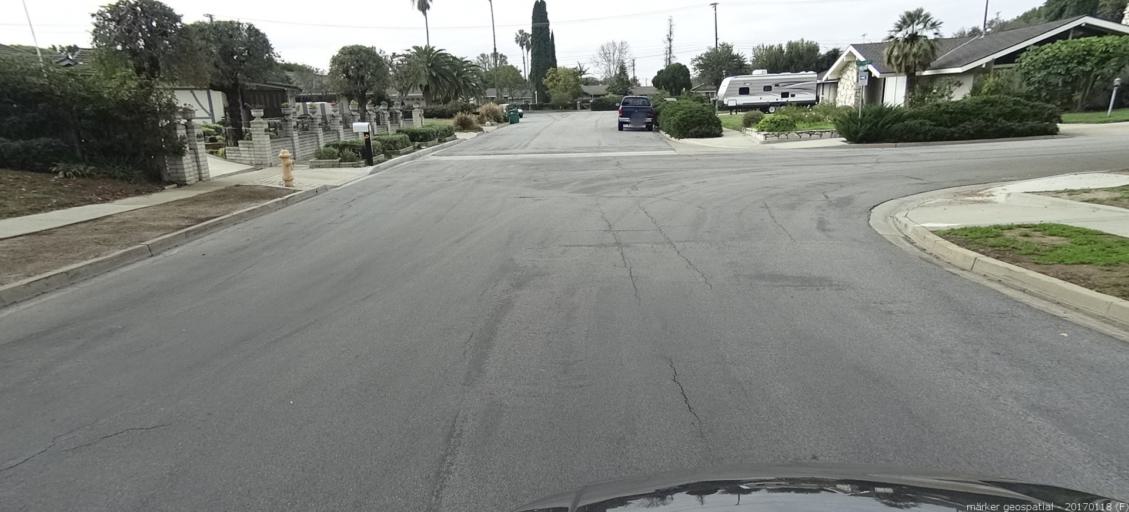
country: US
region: California
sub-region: Orange County
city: North Tustin
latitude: 33.7425
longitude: -117.7990
